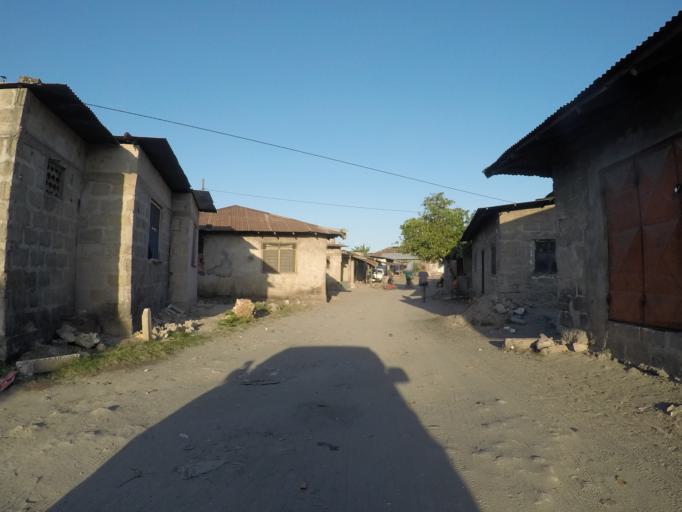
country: TZ
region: Zanzibar Urban/West
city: Zanzibar
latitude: -6.1581
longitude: 39.2166
